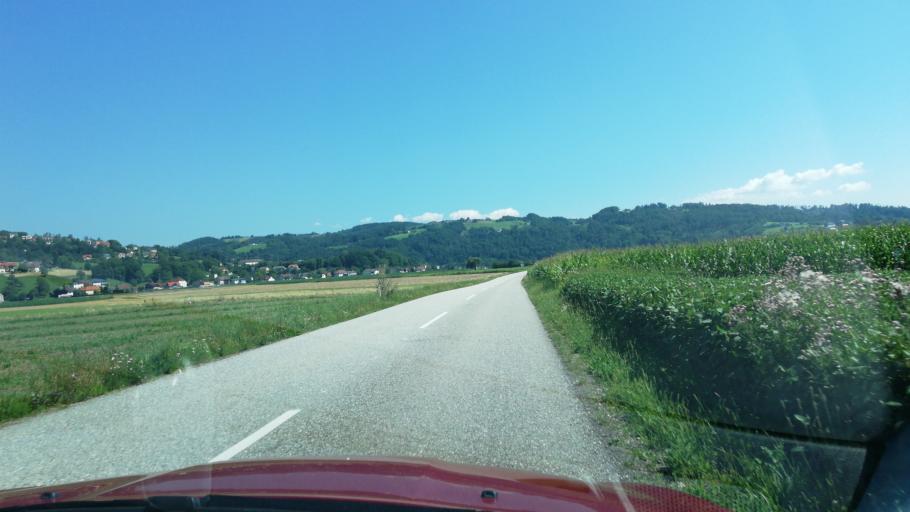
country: AT
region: Upper Austria
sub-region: Politischer Bezirk Urfahr-Umgebung
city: Feldkirchen an der Donau
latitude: 48.3506
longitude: 14.0537
